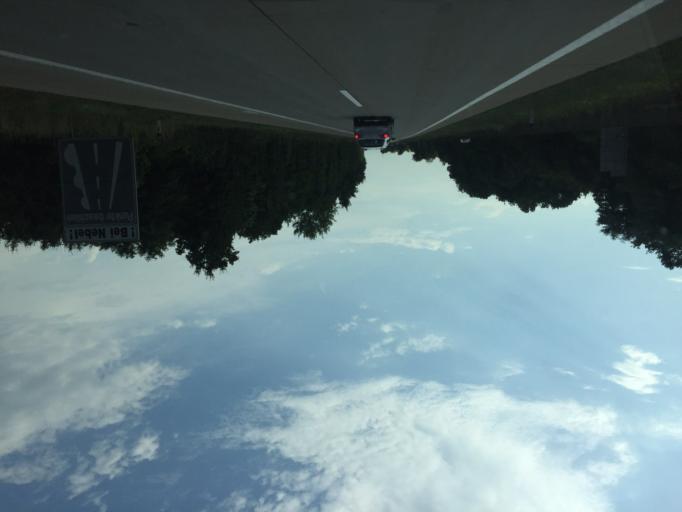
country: AT
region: Styria
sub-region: Politischer Bezirk Leibnitz
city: Obervogau
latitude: 46.7486
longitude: 15.6037
